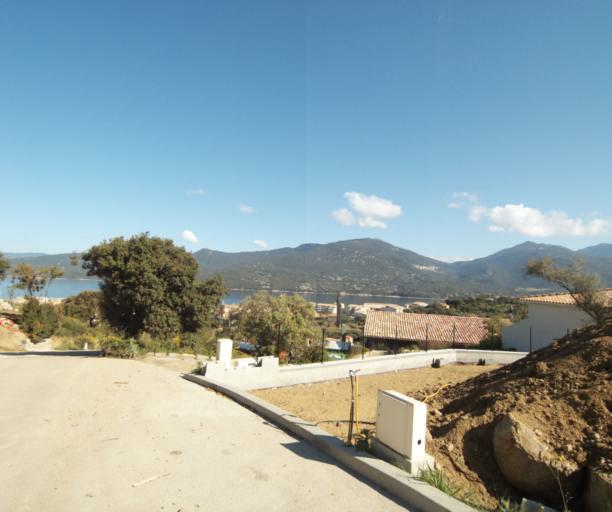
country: FR
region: Corsica
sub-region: Departement de la Corse-du-Sud
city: Propriano
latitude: 41.6689
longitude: 8.9069
